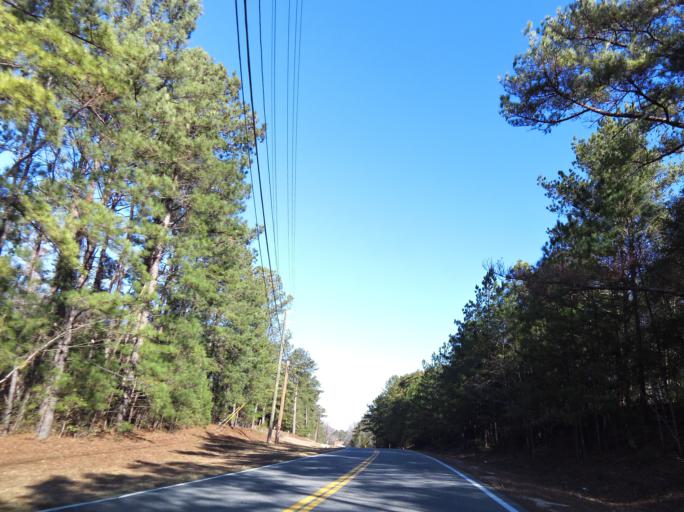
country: US
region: Georgia
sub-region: Bibb County
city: West Point
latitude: 32.7868
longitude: -83.7571
